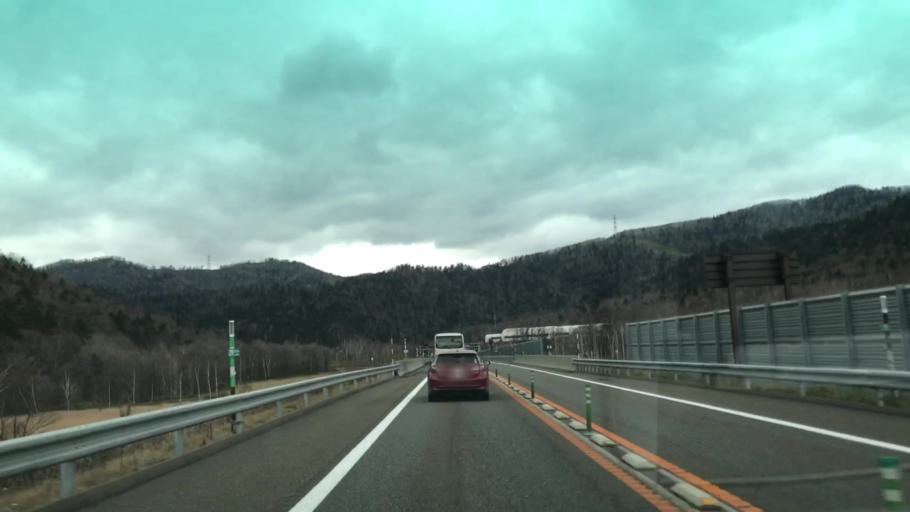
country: JP
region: Hokkaido
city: Shimo-furano
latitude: 43.0631
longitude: 142.5476
